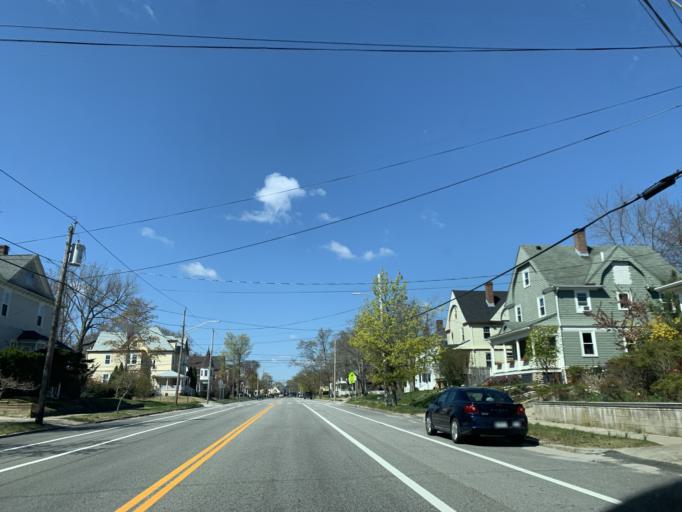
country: US
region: Rhode Island
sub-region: Providence County
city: Cranston
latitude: 41.7790
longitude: -71.3953
